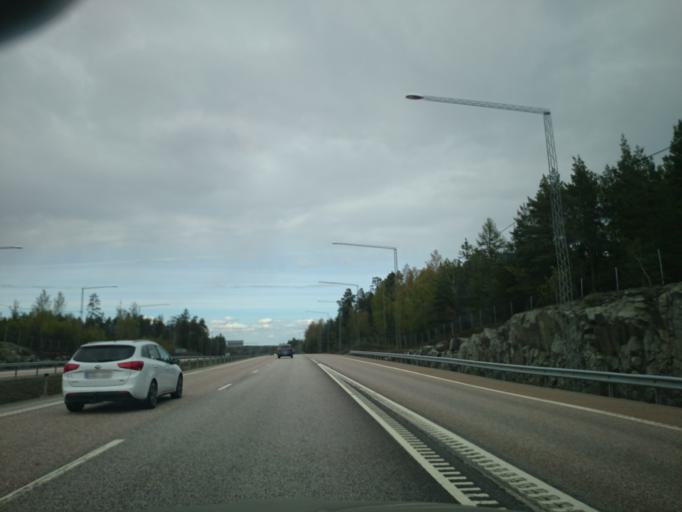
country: SE
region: Stockholm
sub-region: Sigtuna Kommun
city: Rosersberg
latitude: 59.6243
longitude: 17.9014
